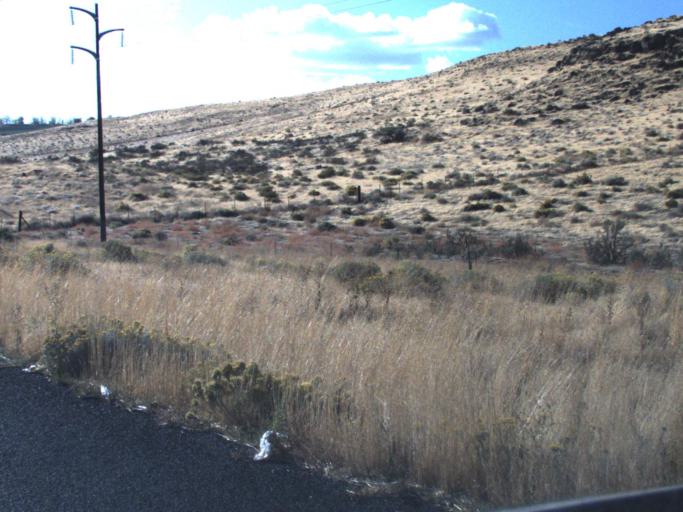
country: US
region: Oregon
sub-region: Morrow County
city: Boardman
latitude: 45.8826
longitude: -119.7266
